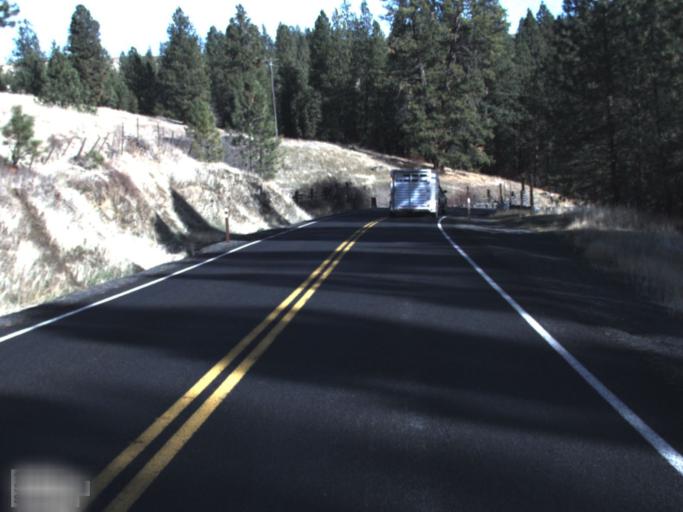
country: US
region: Washington
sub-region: Whitman County
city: Colfax
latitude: 46.9139
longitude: -117.2750
